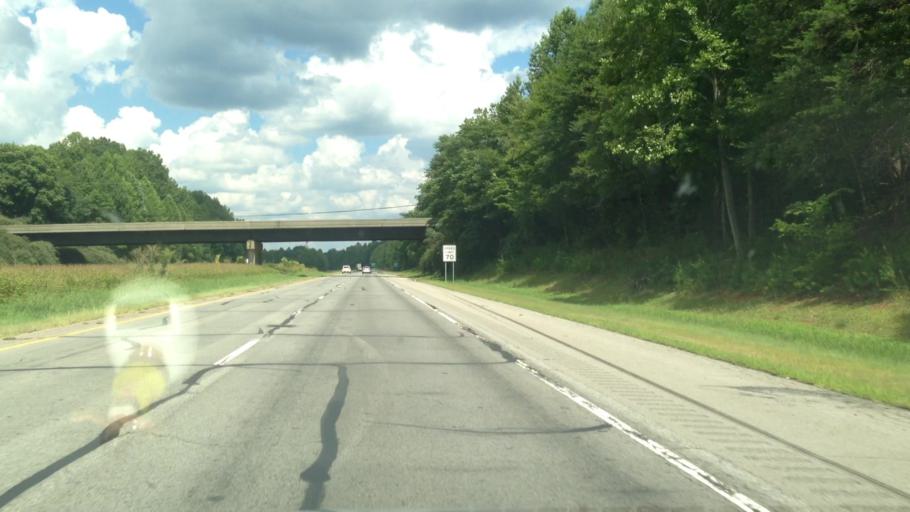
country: US
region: Virginia
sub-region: City of Danville
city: Danville
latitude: 36.4732
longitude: -79.5152
